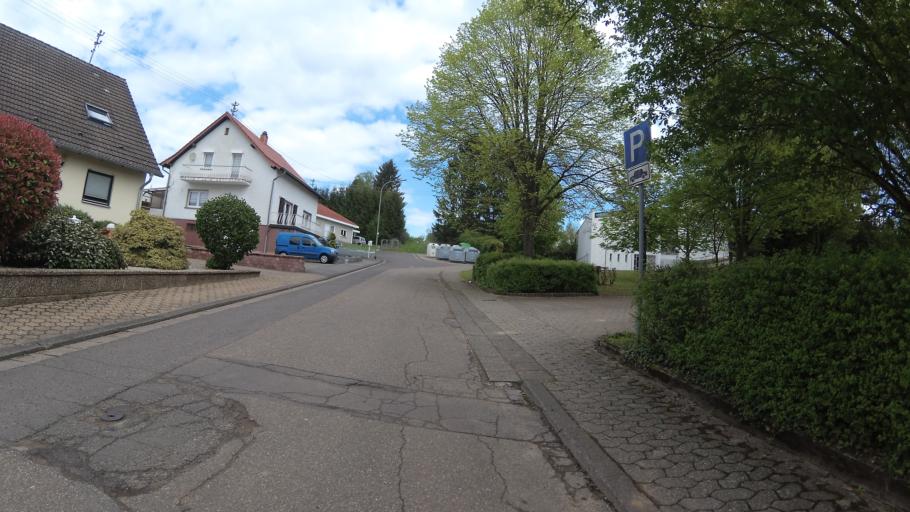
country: DE
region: Saarland
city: Schmelz
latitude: 49.4236
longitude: 6.8378
